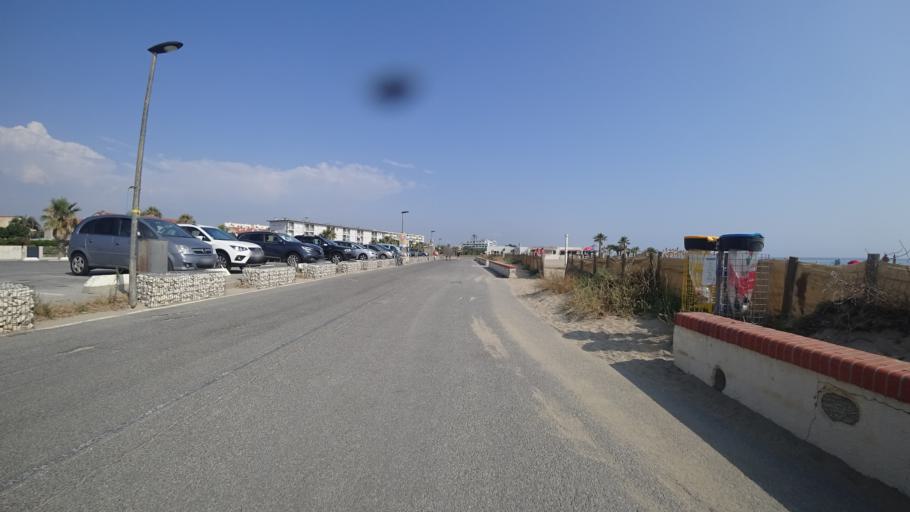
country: FR
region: Languedoc-Roussillon
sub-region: Departement des Pyrenees-Orientales
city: Saint-Cyprien-Plage
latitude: 42.6340
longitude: 3.0353
